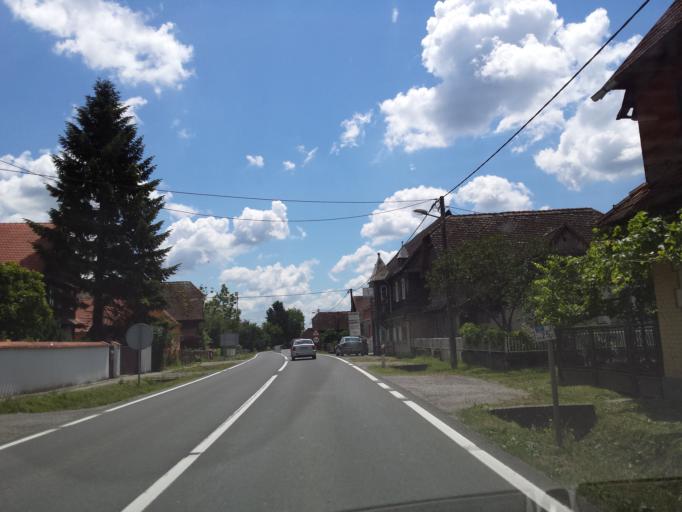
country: HR
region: Sisacko-Moslavacka
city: Lekenik
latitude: 45.5355
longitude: 16.2389
